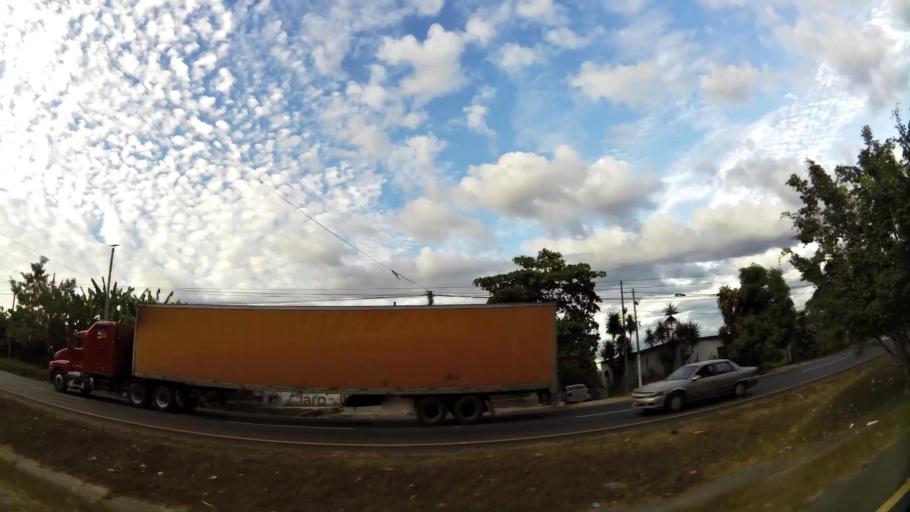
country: SV
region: Cuscatlan
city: Cojutepeque
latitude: 13.7300
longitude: -88.8936
